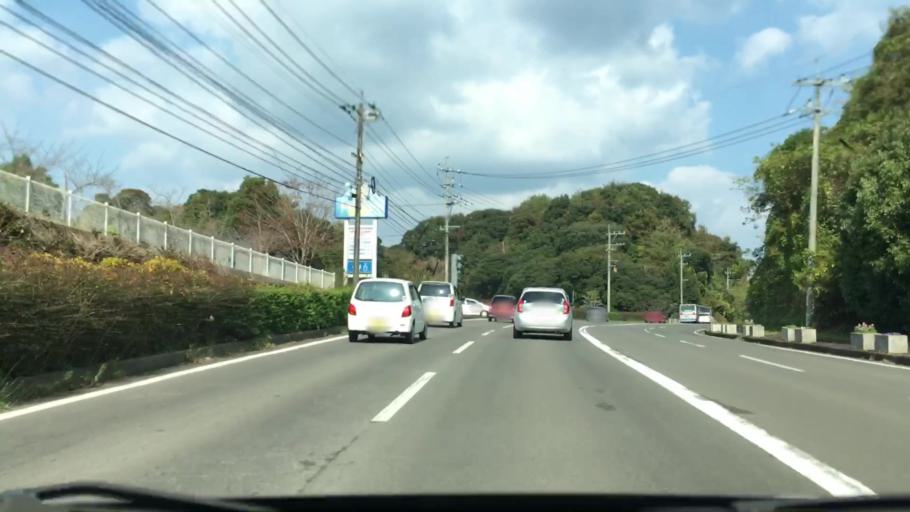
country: JP
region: Nagasaki
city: Sasebo
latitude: 32.9902
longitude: 129.7491
